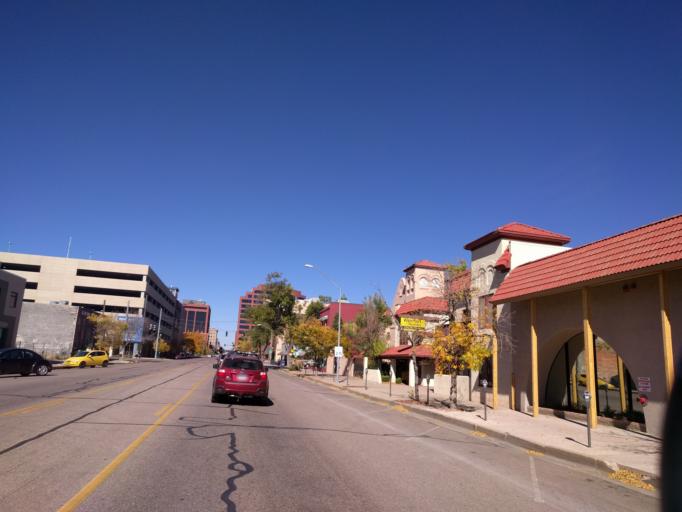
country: US
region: Colorado
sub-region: El Paso County
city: Colorado Springs
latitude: 38.8274
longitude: -104.8238
